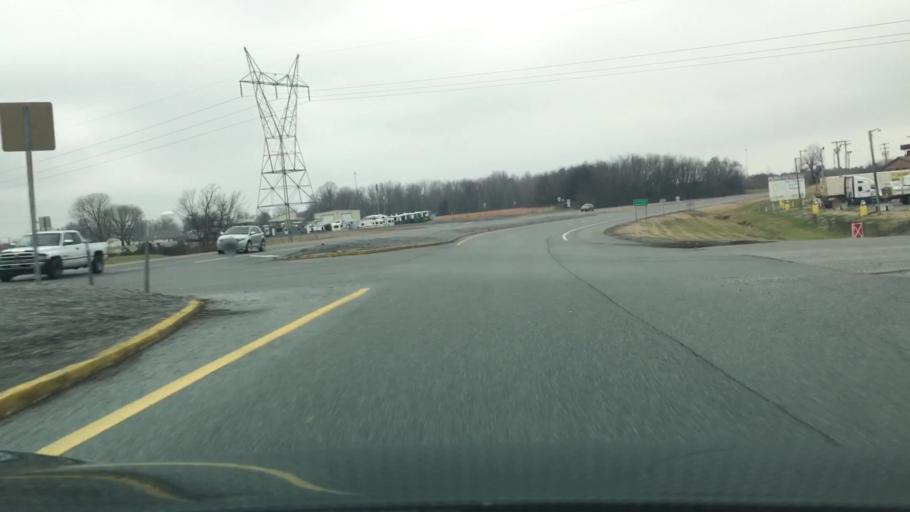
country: US
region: Kentucky
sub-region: McCracken County
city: Reidland
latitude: 36.9888
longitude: -88.5044
